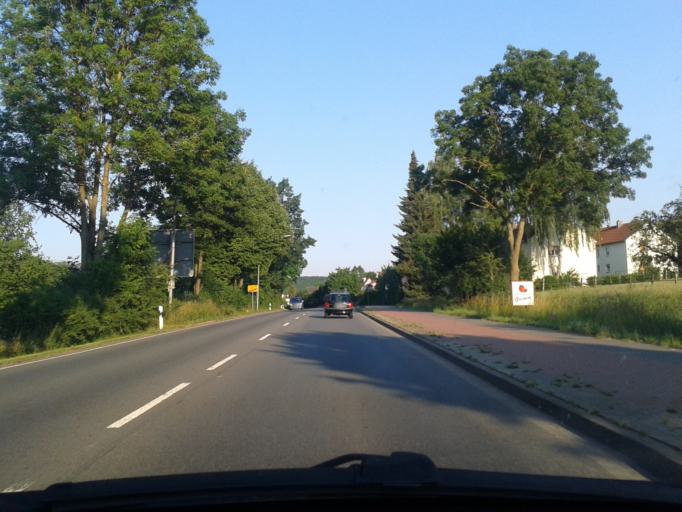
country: DE
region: North Rhine-Westphalia
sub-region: Regierungsbezirk Detmold
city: Detmold
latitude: 51.9120
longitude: 8.9130
